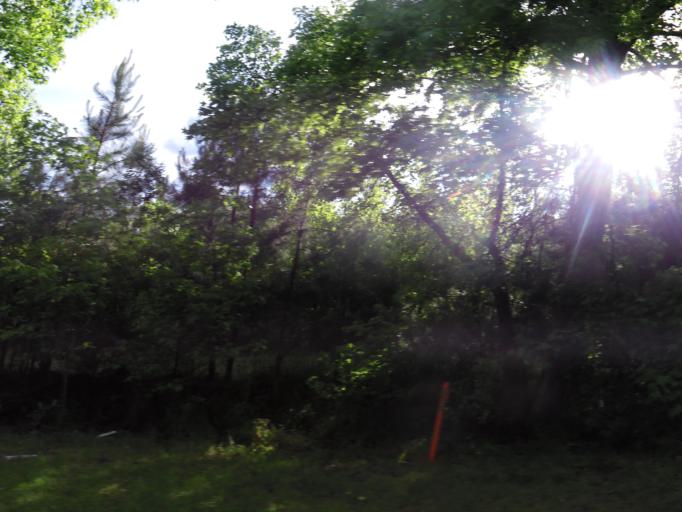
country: US
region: South Carolina
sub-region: Jasper County
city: Ridgeland
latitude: 32.5134
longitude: -81.1436
